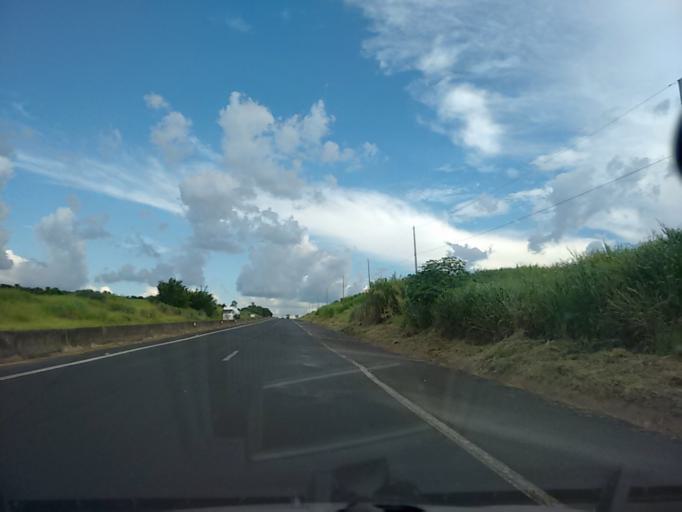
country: BR
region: Sao Paulo
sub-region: Marilia
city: Marilia
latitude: -22.2198
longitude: -49.8351
